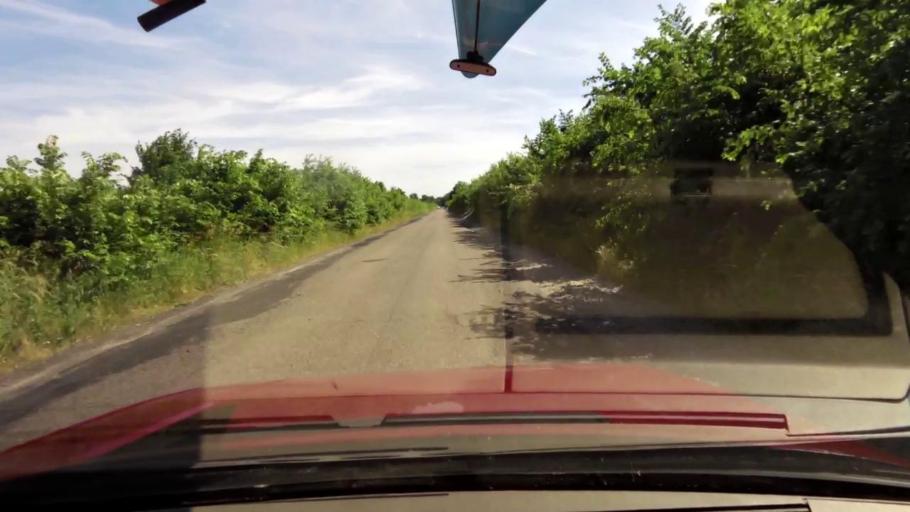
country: PL
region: Pomeranian Voivodeship
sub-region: Powiat slupski
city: Kobylnica
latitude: 54.3629
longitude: 16.9673
